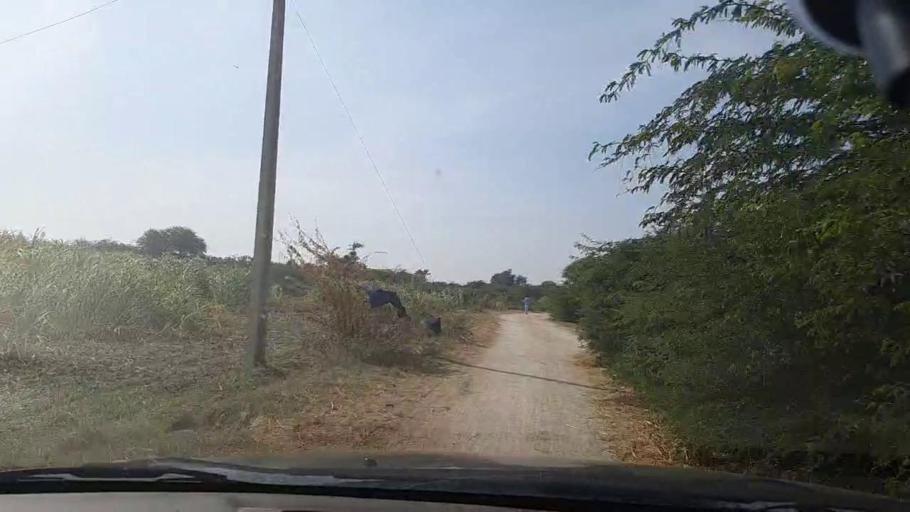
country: PK
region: Sindh
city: Mirpur Batoro
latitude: 24.7367
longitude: 68.2692
